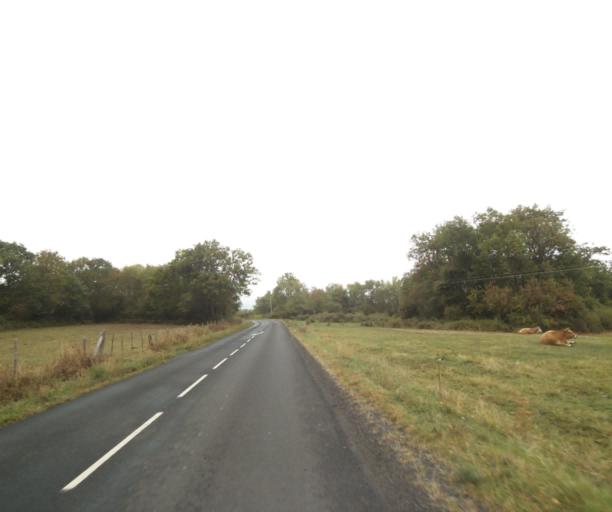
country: FR
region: Auvergne
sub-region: Departement du Puy-de-Dome
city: Chanonat
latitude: 45.7119
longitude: 3.0872
